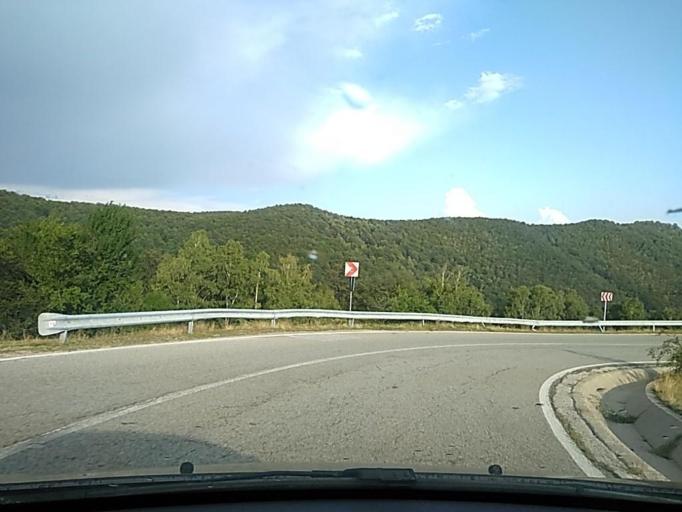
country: RO
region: Gorj
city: Novaci-Straini
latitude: 45.2187
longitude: 23.6985
